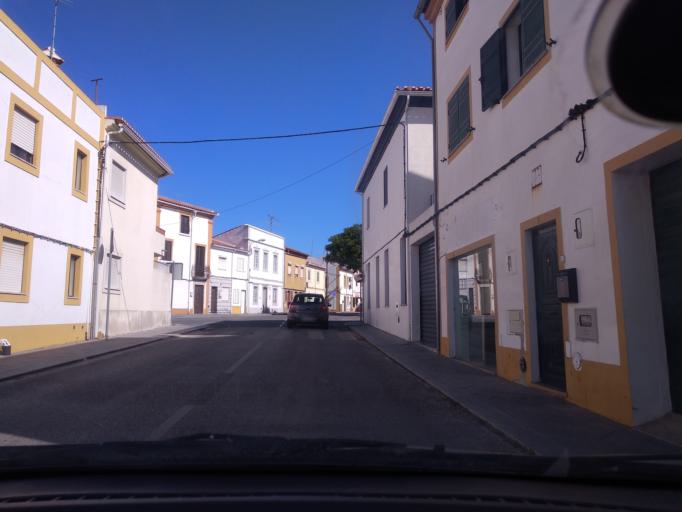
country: PT
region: Portalegre
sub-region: Nisa
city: Nisa
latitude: 39.5149
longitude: -7.6490
